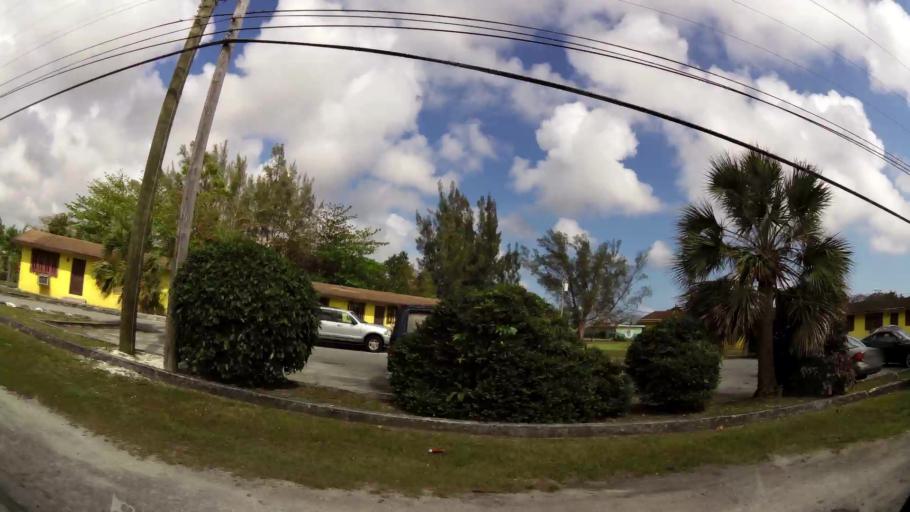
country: BS
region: Freeport
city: Freeport
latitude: 26.5369
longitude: -78.6924
